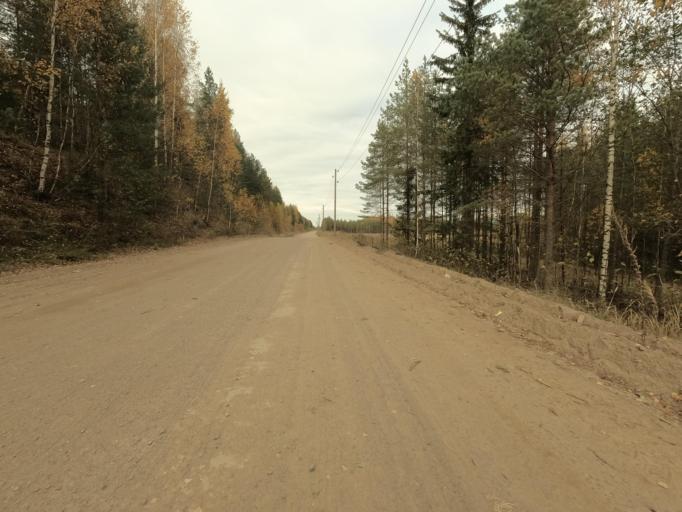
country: RU
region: Leningrad
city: Priladozhskiy
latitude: 59.6927
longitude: 31.3611
